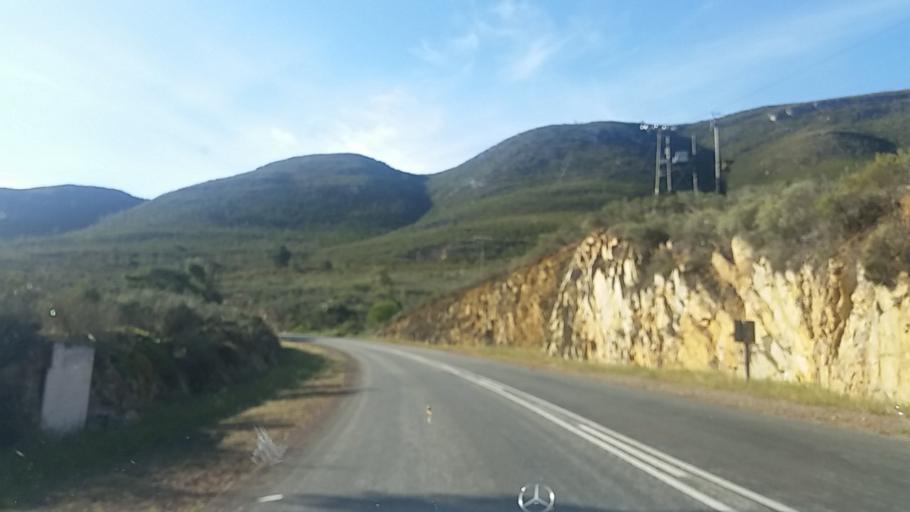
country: ZA
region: Western Cape
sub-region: Eden District Municipality
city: Knysna
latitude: -33.7617
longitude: 22.9626
